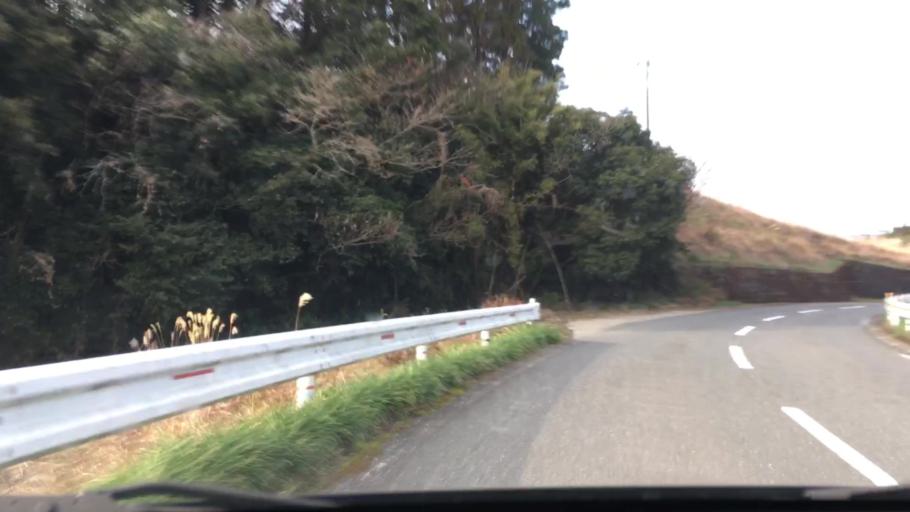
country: JP
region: Miyazaki
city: Nichinan
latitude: 31.6172
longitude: 131.3354
